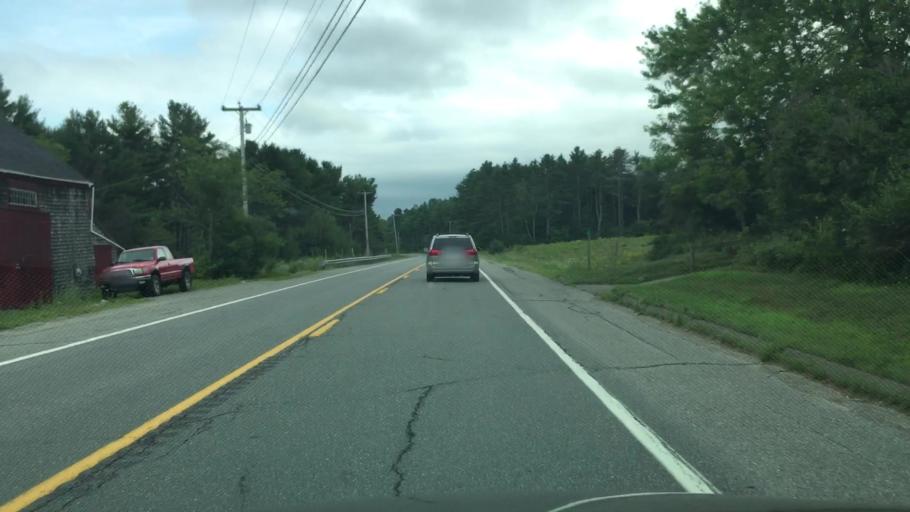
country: US
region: Maine
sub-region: Waldo County
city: Stockton Springs
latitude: 44.5472
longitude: -68.8642
